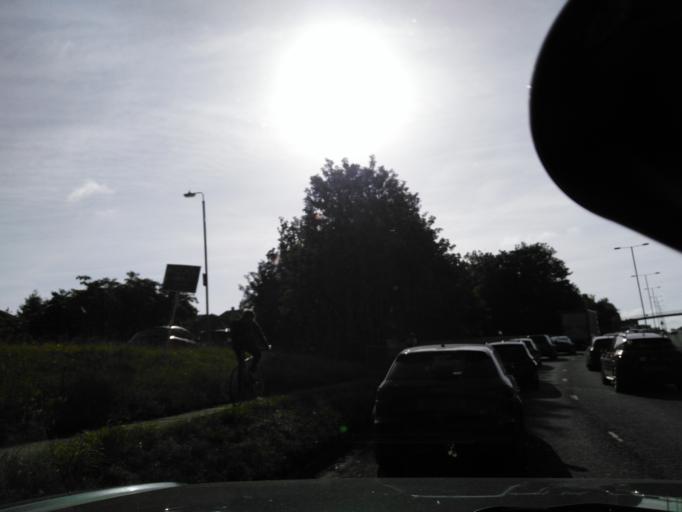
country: GB
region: England
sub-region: Wiltshire
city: Salisbury
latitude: 51.0768
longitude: -1.7938
